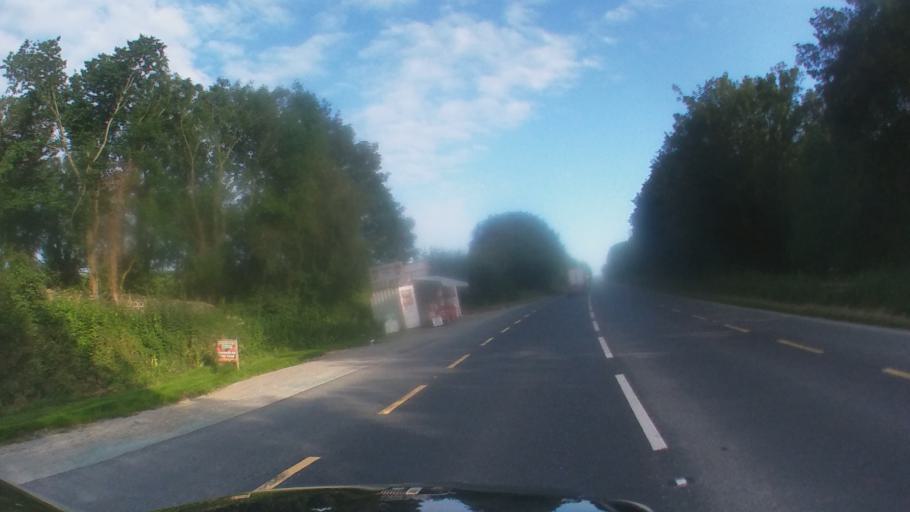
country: IE
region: Leinster
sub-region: Loch Garman
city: Enniscorthy
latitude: 52.4870
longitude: -6.5655
